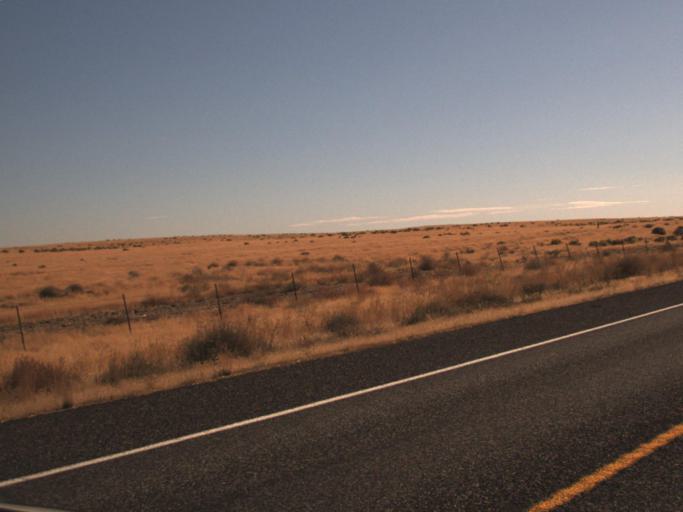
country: US
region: Washington
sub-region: Benton County
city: Benton City
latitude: 46.4424
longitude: -119.4921
